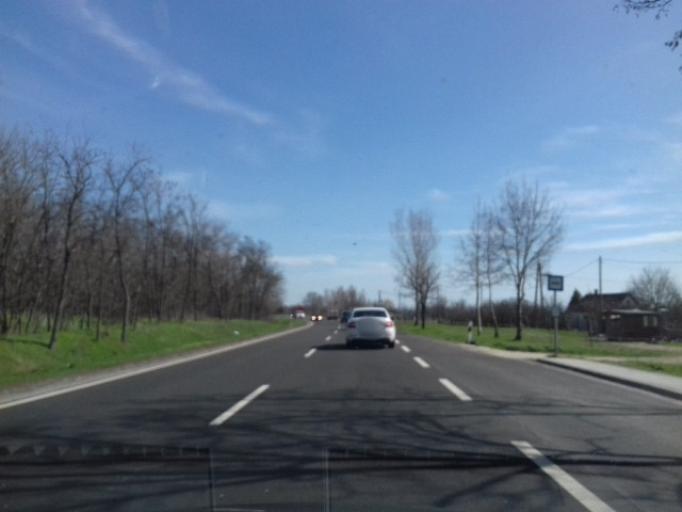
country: HU
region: Bacs-Kiskun
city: Nyarlorinc
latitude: 46.8711
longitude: 19.8543
